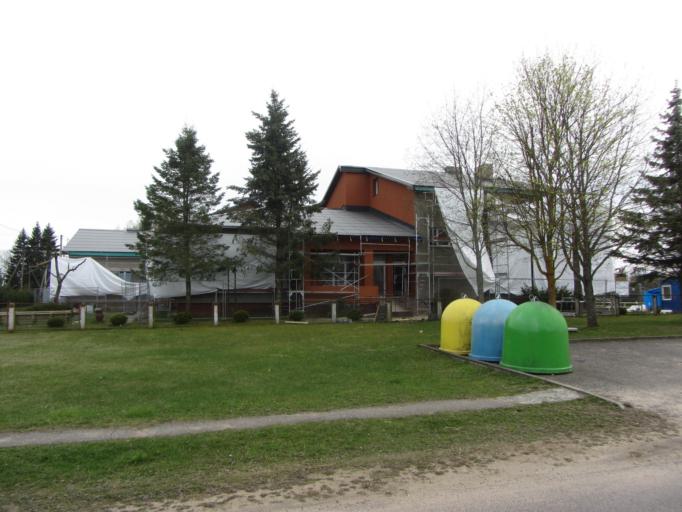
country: LT
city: Zarasai
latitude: 55.5783
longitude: 26.1288
